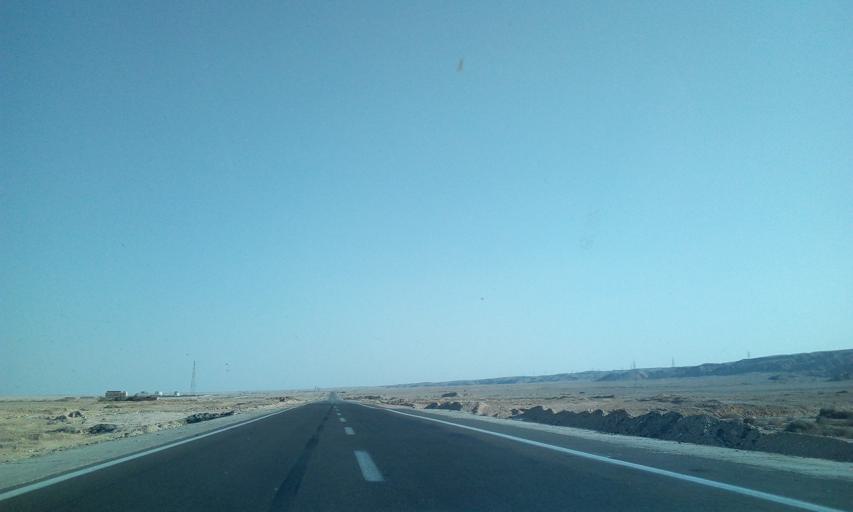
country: EG
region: As Suways
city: Ain Sukhna
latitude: 28.9793
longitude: 32.6169
